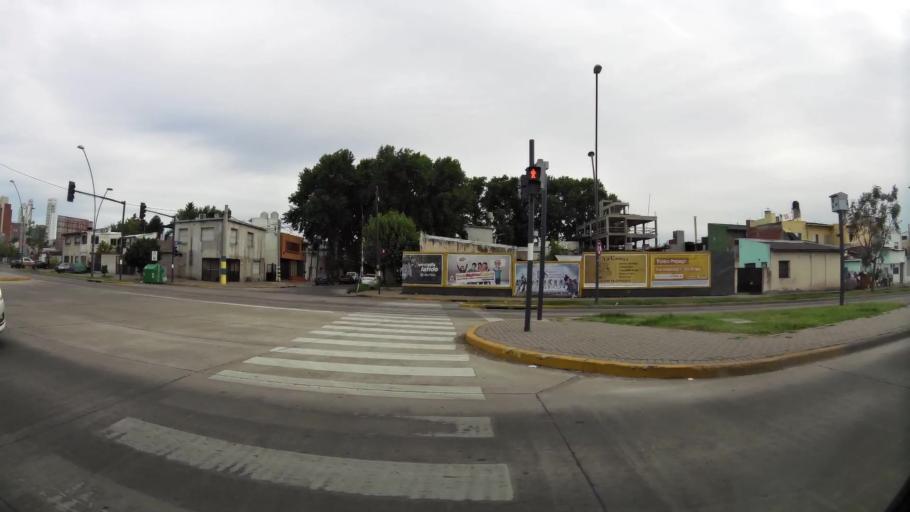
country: AR
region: Santa Fe
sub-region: Departamento de Rosario
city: Rosario
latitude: -32.9218
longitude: -60.6698
